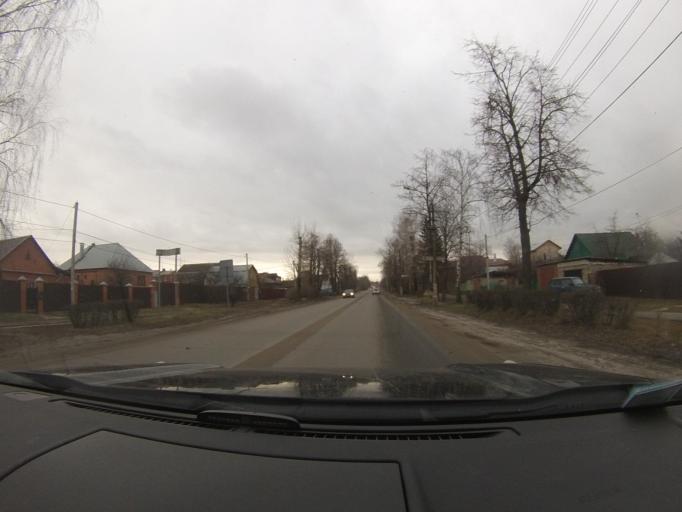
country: RU
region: Moskovskaya
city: Lopatinskiy
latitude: 55.3256
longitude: 38.6978
